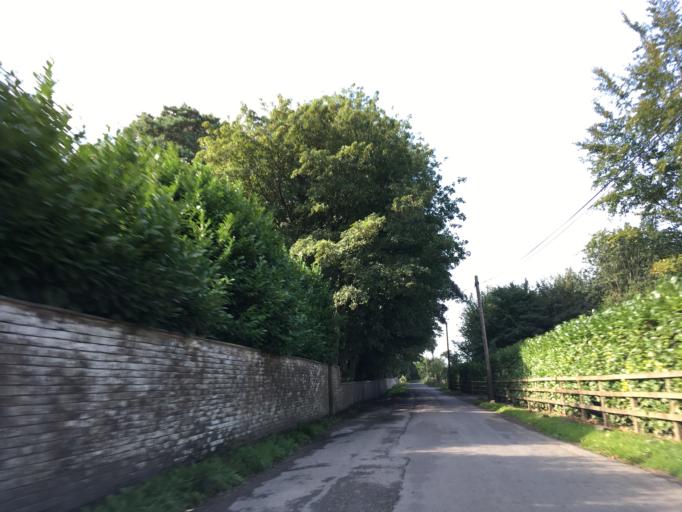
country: GB
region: England
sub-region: South Gloucestershire
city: Horton
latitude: 51.5228
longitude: -2.3572
